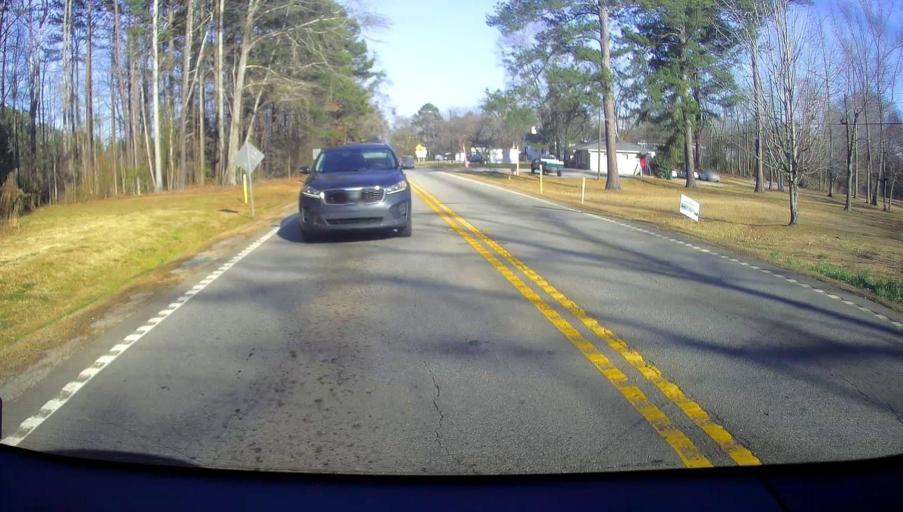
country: US
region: Georgia
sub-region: Henry County
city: Locust Grove
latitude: 33.3229
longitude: -84.0395
